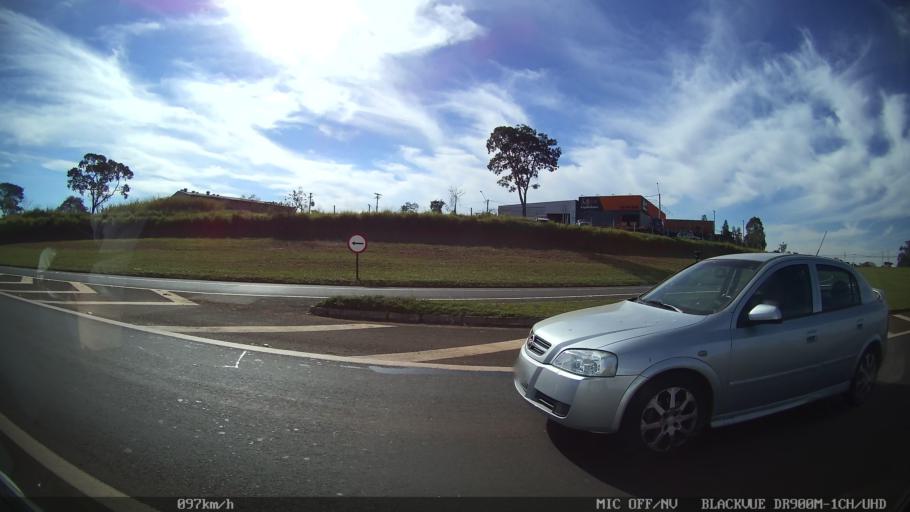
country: BR
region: Sao Paulo
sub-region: Araraquara
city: Araraquara
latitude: -21.8134
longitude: -48.1621
